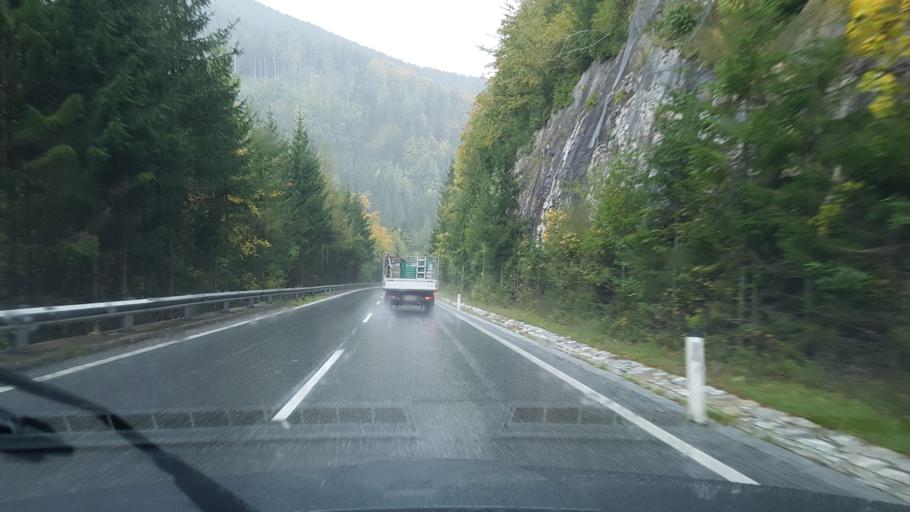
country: AT
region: Styria
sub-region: Politischer Bezirk Voitsberg
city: Salla
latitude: 47.1055
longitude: 14.9542
